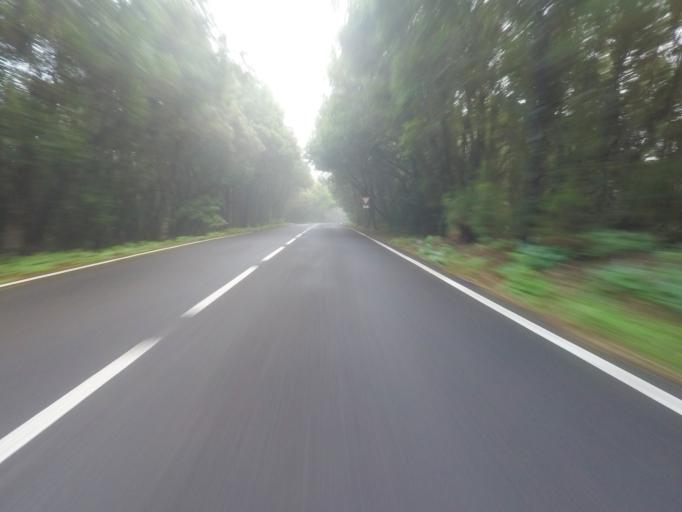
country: ES
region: Canary Islands
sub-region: Provincia de Santa Cruz de Tenerife
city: Alajero
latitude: 28.1133
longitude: -17.2181
